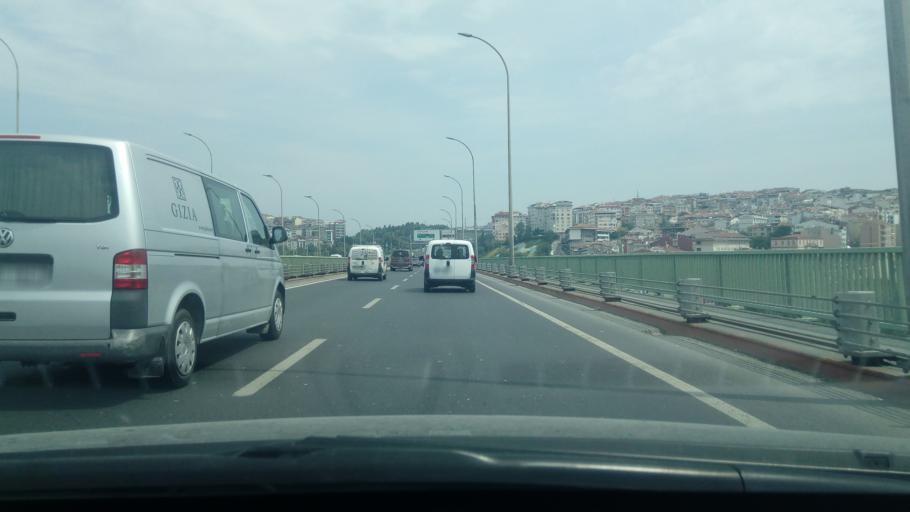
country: TR
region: Istanbul
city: Istanbul
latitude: 41.0414
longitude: 28.9405
